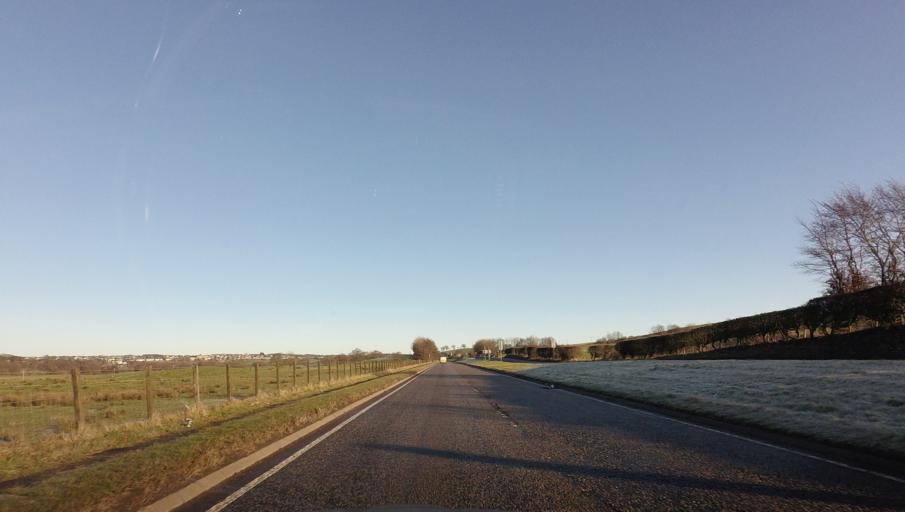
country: GB
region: Scotland
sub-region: North Lanarkshire
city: Shotts
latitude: 55.8042
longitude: -3.8210
